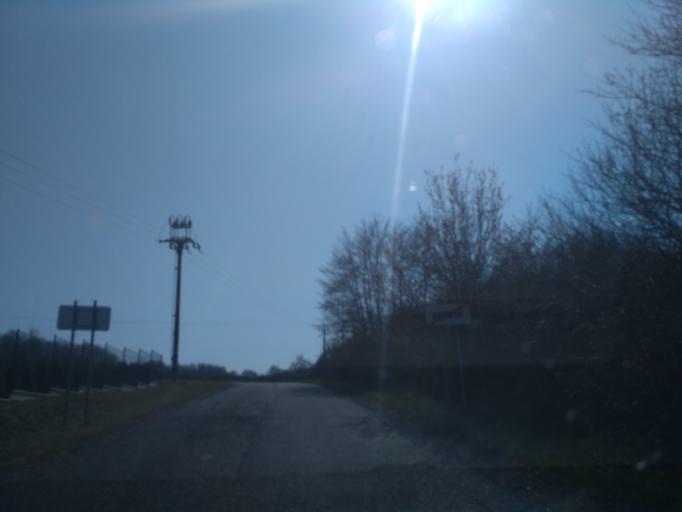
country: SK
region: Presovsky
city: Vranov nad Topl'ou
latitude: 48.8227
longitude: 21.6368
